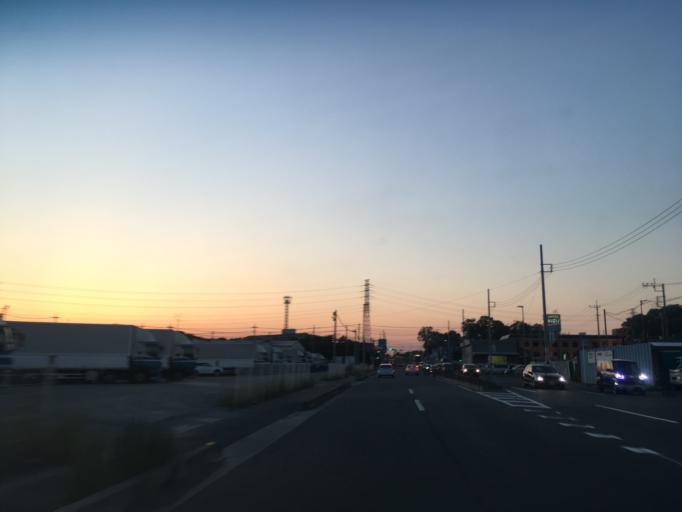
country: JP
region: Saitama
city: Tokorozawa
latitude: 35.7962
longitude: 139.5029
